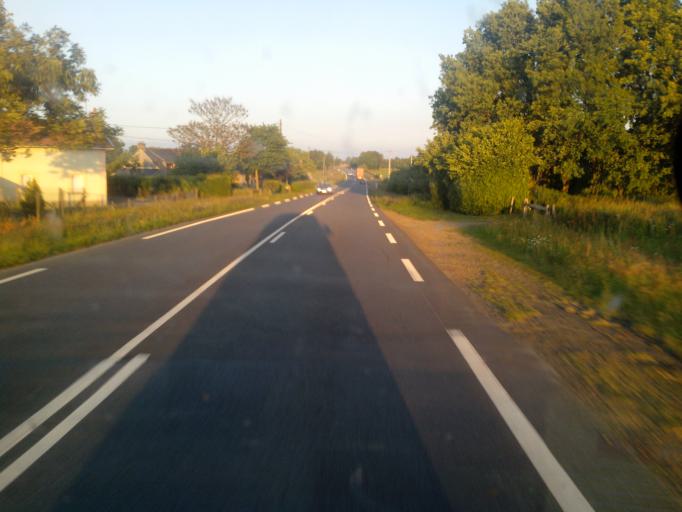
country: FR
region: Brittany
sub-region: Departement d'Ille-et-Vilaine
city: Saint-Etienne-en-Cogles
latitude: 48.3964
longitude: -1.2967
